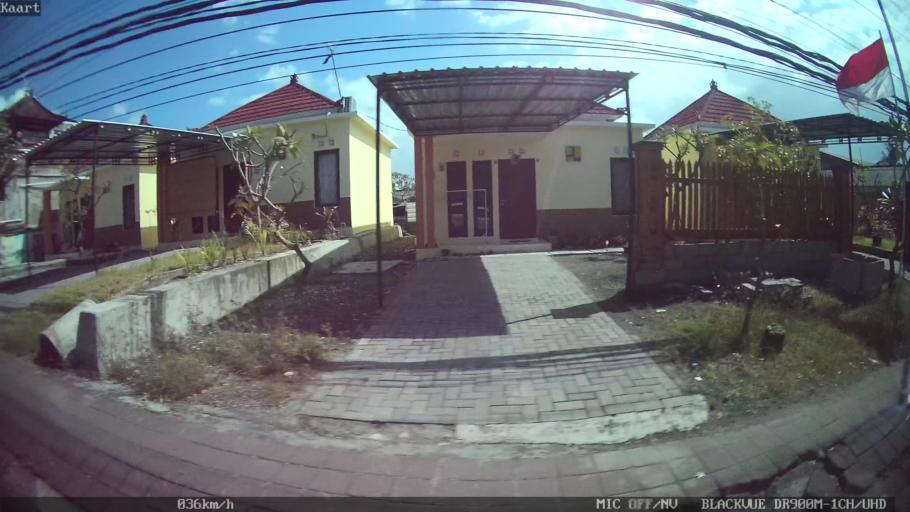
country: ID
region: Bali
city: Kuta
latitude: -8.6723
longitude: 115.1700
